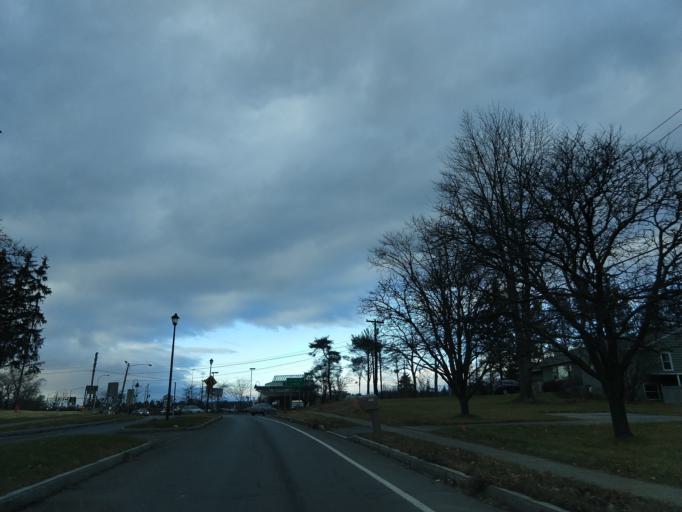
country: US
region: New York
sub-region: Tompkins County
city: Lansing
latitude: 42.4775
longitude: -76.4818
